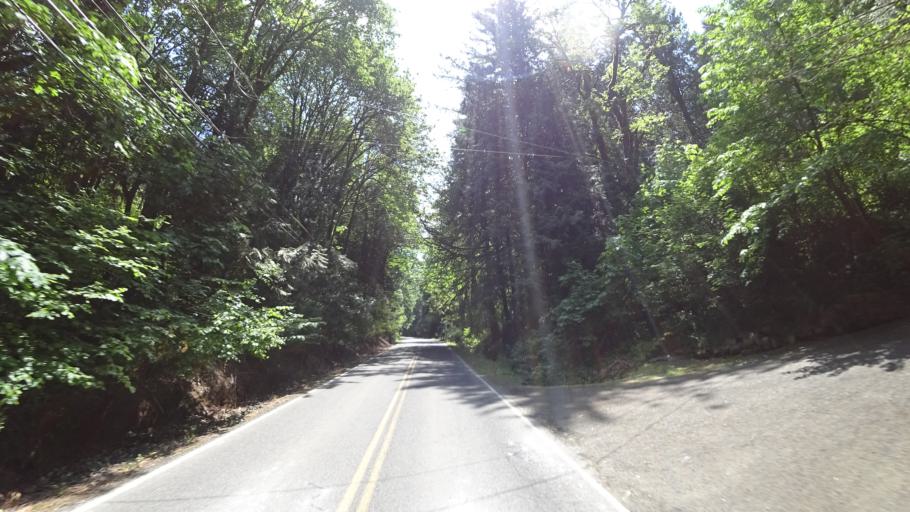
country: US
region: Oregon
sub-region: Clackamas County
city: Happy Valley
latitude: 45.4706
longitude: -122.5115
